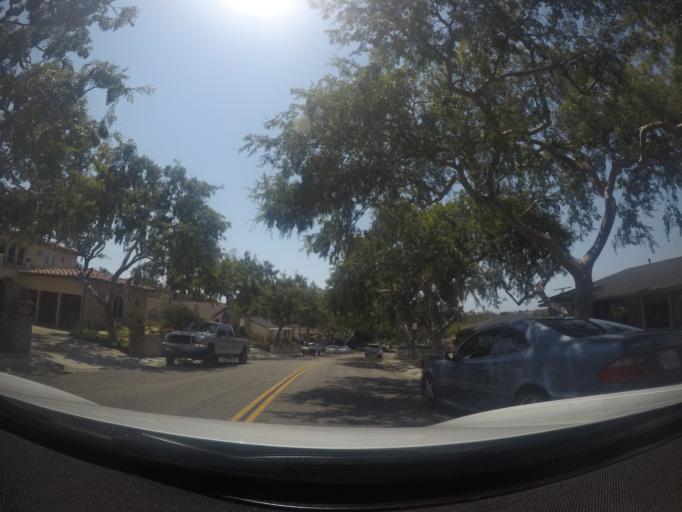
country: US
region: California
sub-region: Los Angeles County
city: Palos Verdes Estates
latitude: 33.8159
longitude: -118.3728
